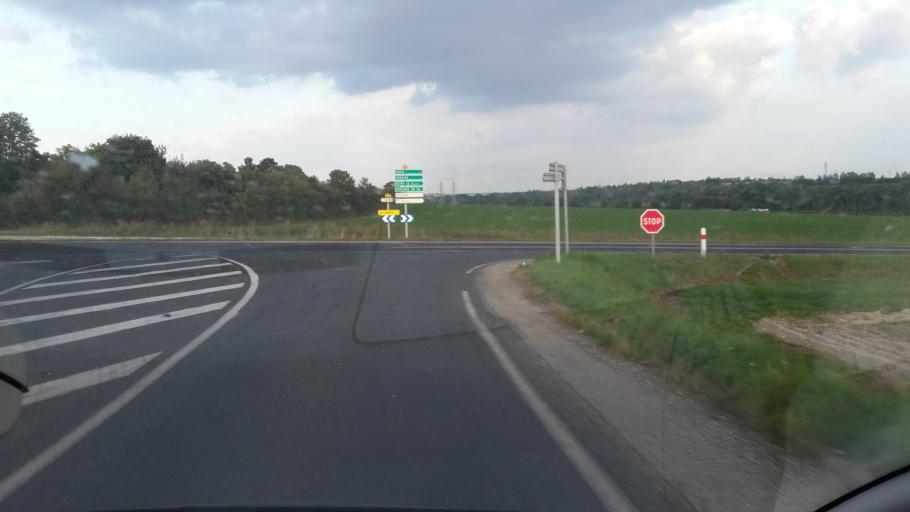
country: FR
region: Champagne-Ardenne
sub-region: Departement de la Marne
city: Fere-Champenoise
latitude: 48.7649
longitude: 3.9966
